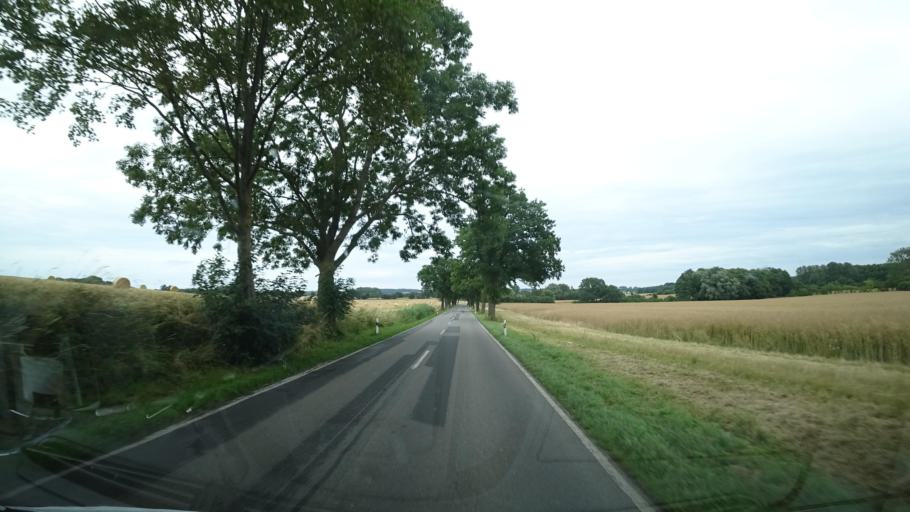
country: DE
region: Mecklenburg-Vorpommern
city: Putbus
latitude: 54.3560
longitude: 13.4910
